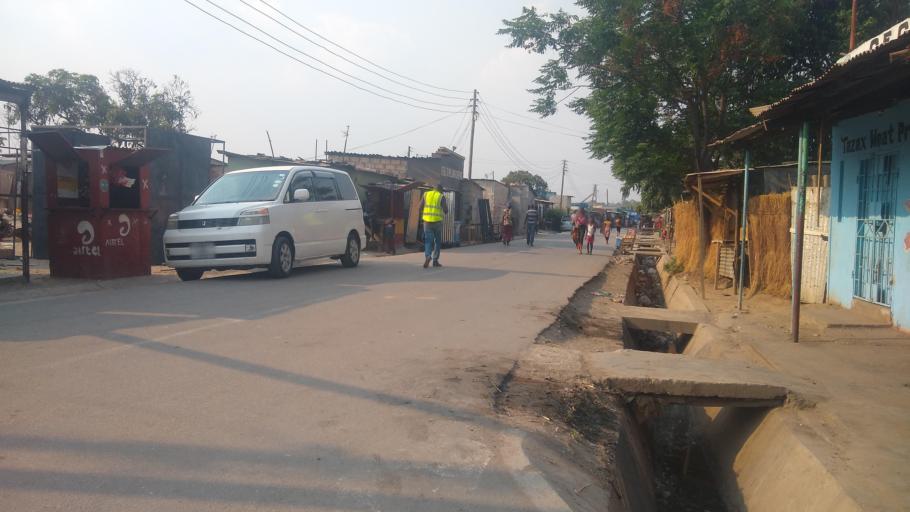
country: ZM
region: Lusaka
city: Lusaka
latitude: -15.4453
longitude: 28.3798
